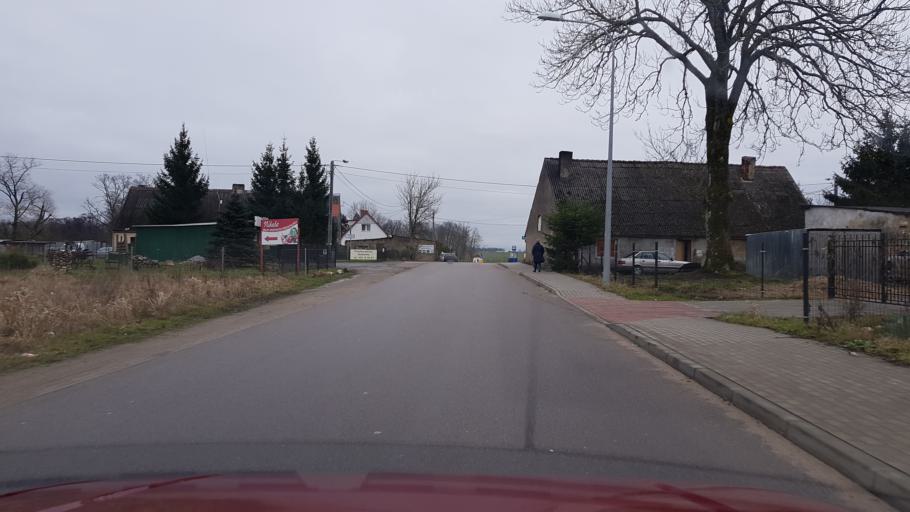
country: PL
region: West Pomeranian Voivodeship
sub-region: Powiat koszalinski
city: Mielno
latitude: 54.1632
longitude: 16.0373
